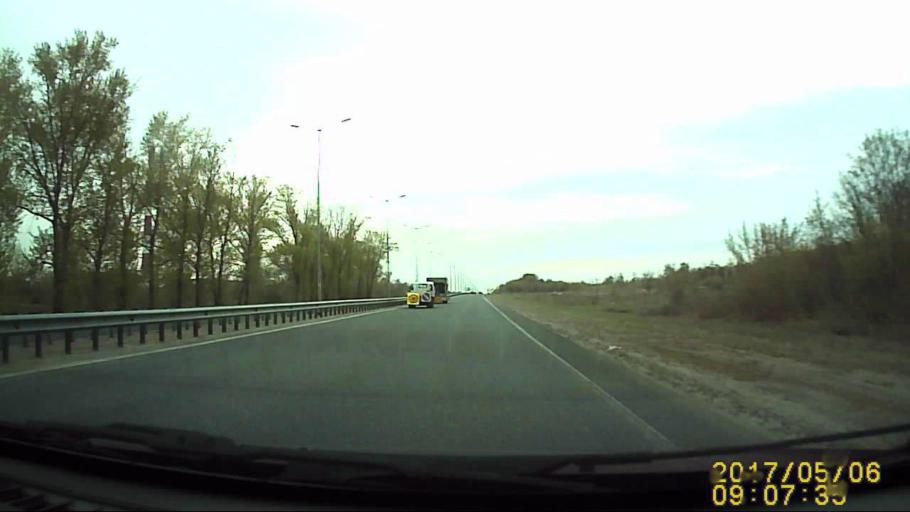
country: RU
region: Ulyanovsk
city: Mirnyy
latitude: 54.3421
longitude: 48.6094
